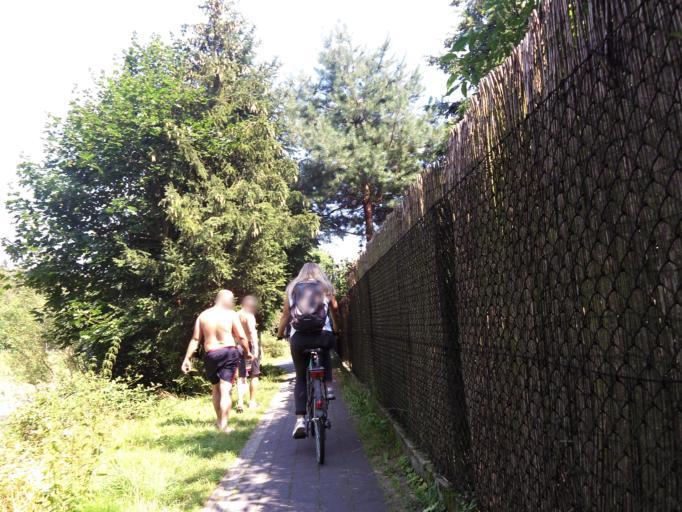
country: PL
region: Silesian Voivodeship
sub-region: Powiat zywiecki
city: Wegierska Gorka
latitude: 49.6089
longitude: 19.1116
